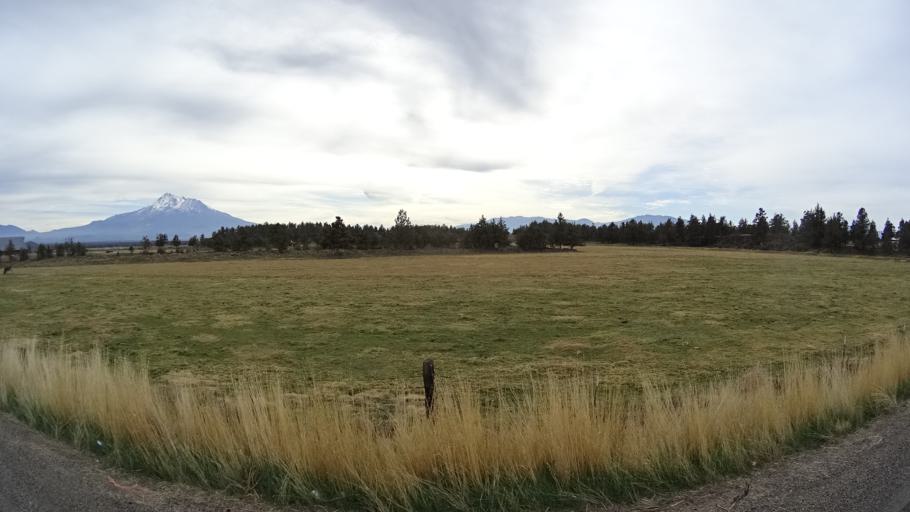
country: US
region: California
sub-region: Siskiyou County
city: Montague
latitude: 41.6241
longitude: -122.4165
